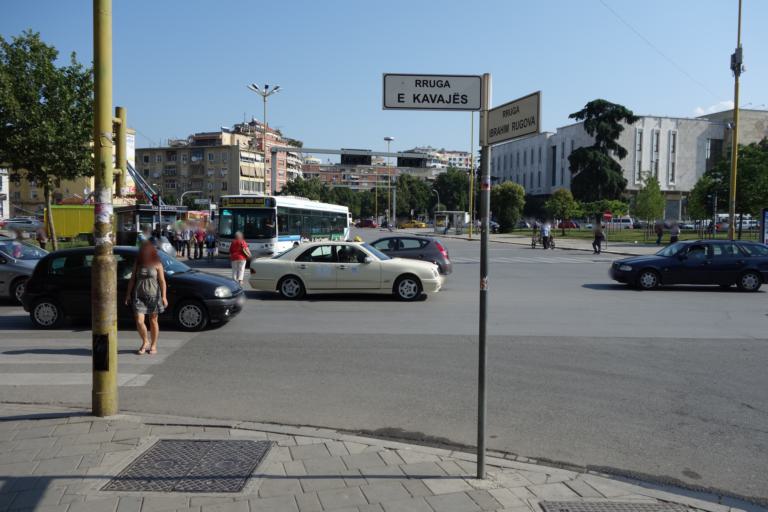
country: AL
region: Tirane
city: Tirana
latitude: 41.3279
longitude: 19.8160
